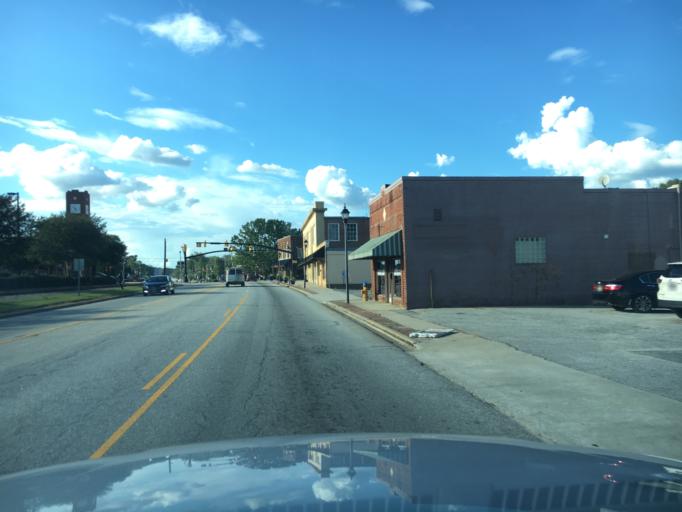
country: US
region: South Carolina
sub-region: Greenville County
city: Simpsonville
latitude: 34.7367
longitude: -82.2549
